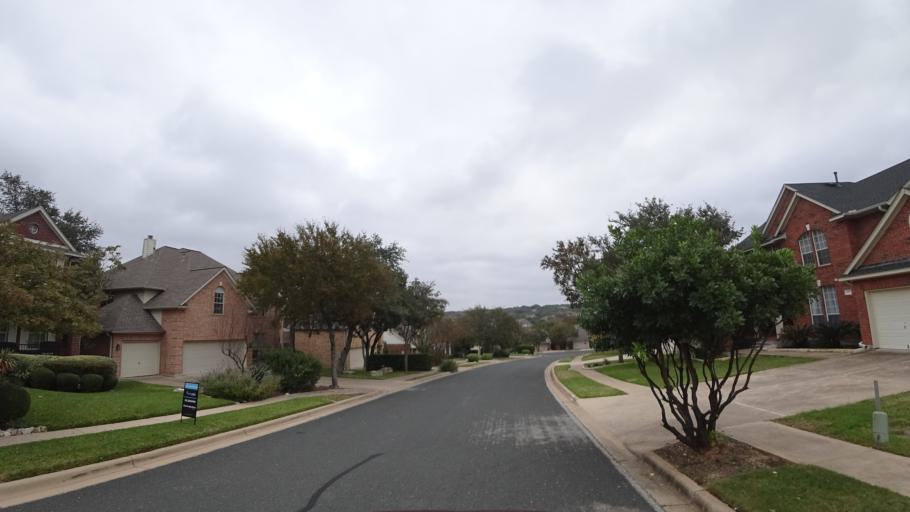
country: US
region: Texas
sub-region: Williamson County
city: Anderson Mill
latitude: 30.4378
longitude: -97.8173
